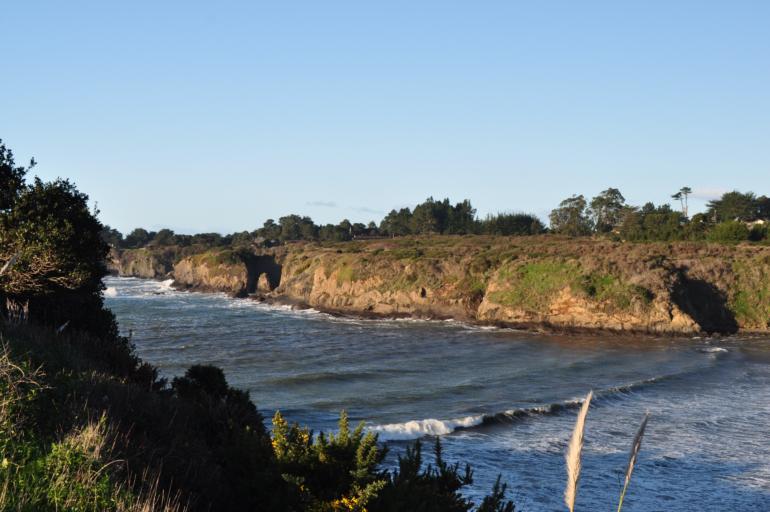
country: US
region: California
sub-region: Mendocino County
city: Fort Bragg
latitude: 39.3597
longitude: -123.8180
